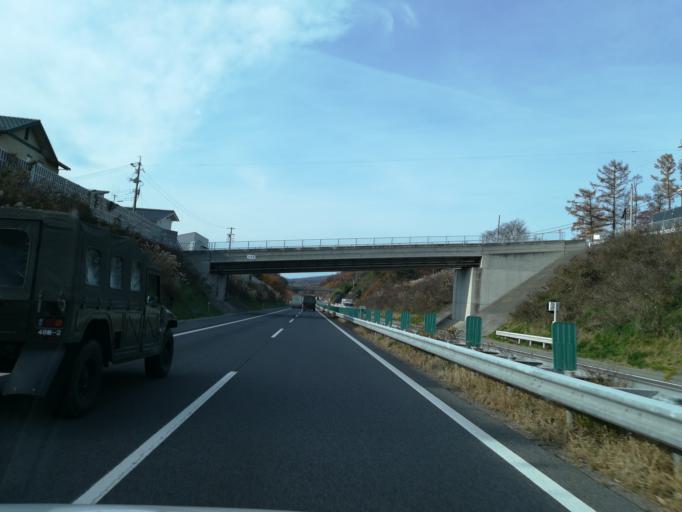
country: JP
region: Nagano
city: Komoro
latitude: 36.3339
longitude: 138.4454
